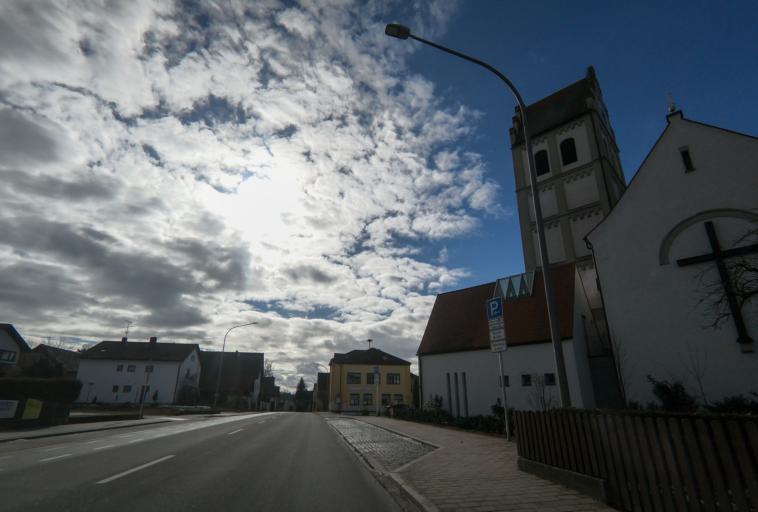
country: DE
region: Bavaria
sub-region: Lower Bavaria
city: Mallersdorf-Pfaffenberg
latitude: 48.7398
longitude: 12.1926
